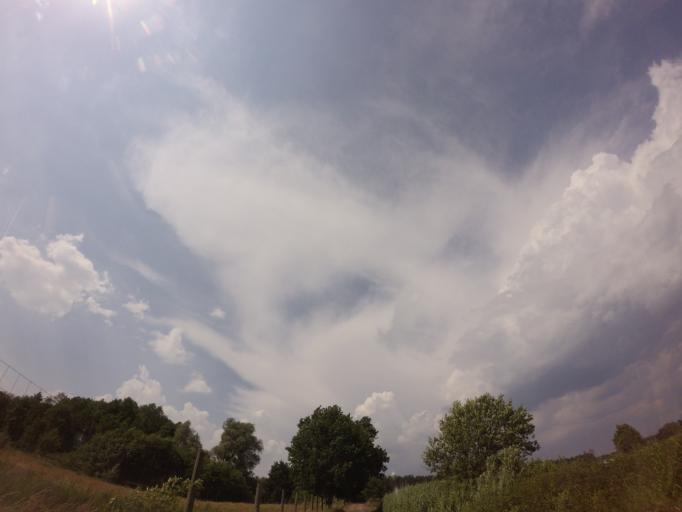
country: PL
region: West Pomeranian Voivodeship
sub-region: Powiat choszczenski
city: Bierzwnik
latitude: 53.1201
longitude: 15.5993
